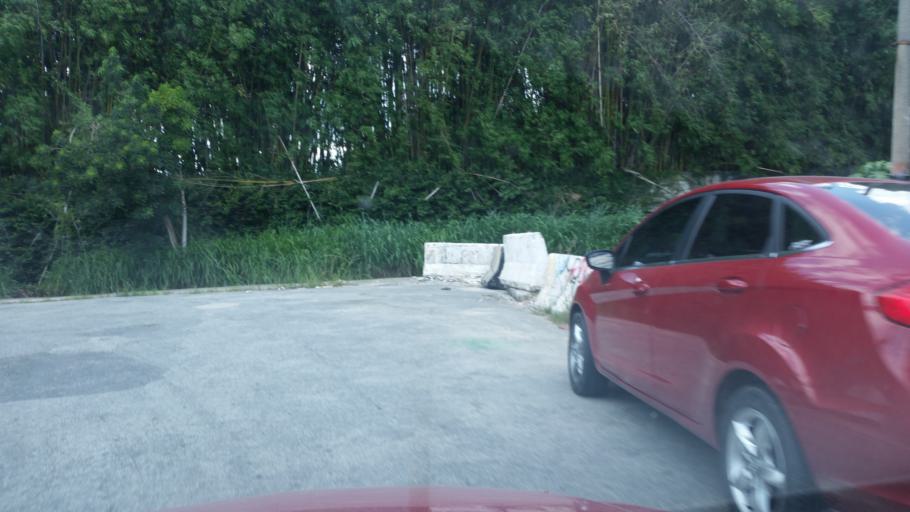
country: BR
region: Sao Paulo
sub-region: Diadema
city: Diadema
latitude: -23.6635
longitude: -46.7057
